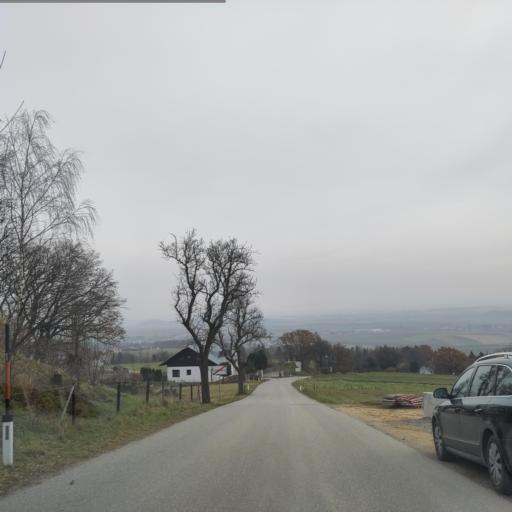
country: AT
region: Lower Austria
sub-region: Politischer Bezirk Sankt Polten
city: Neidling
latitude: 48.2431
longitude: 15.5300
